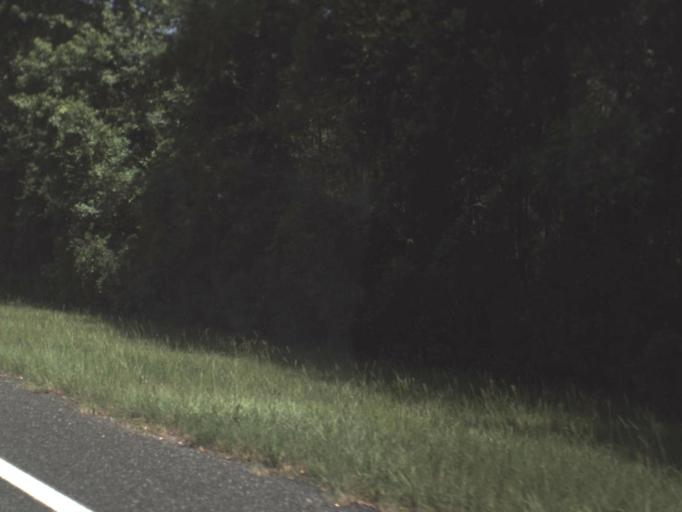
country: US
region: Florida
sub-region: Taylor County
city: Steinhatchee
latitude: 29.6814
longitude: -83.2607
